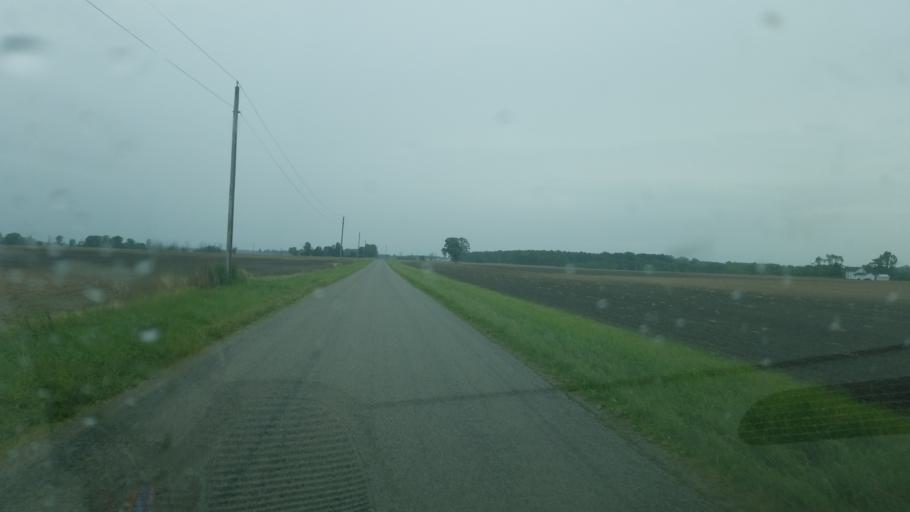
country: US
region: Ohio
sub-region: Marion County
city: Marion
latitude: 40.6987
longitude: -83.0683
